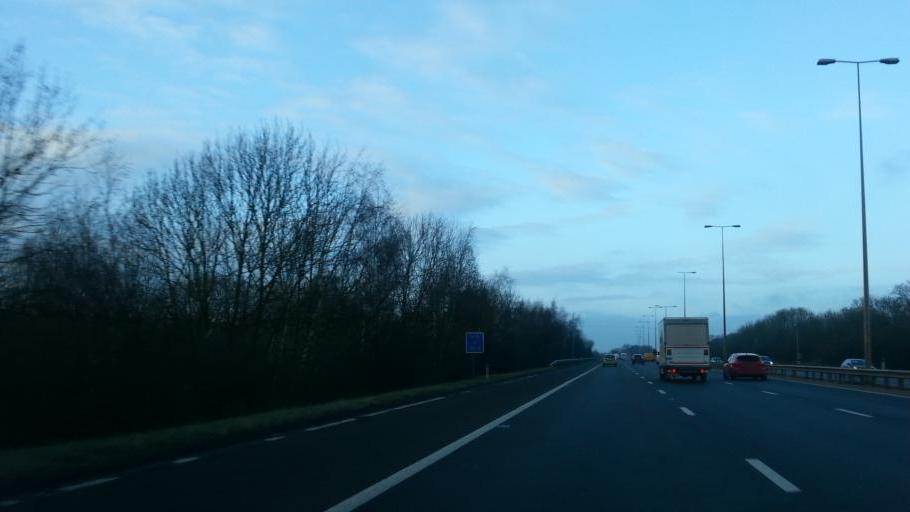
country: GB
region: England
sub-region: Worcestershire
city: Kempsey
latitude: 52.1223
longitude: -2.1994
